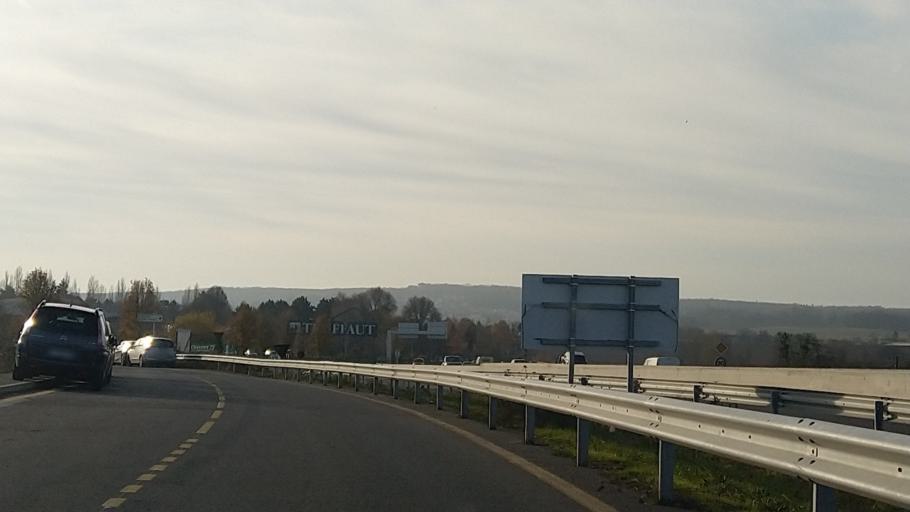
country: FR
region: Ile-de-France
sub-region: Departement du Val-d'Oise
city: Moisselles
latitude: 49.0589
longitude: 2.3323
